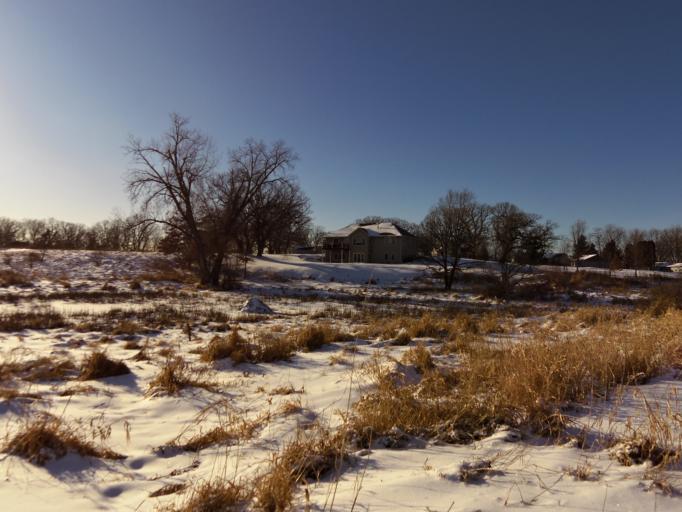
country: US
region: Minnesota
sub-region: Washington County
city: Lake Elmo
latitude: 44.9933
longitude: -92.9110
